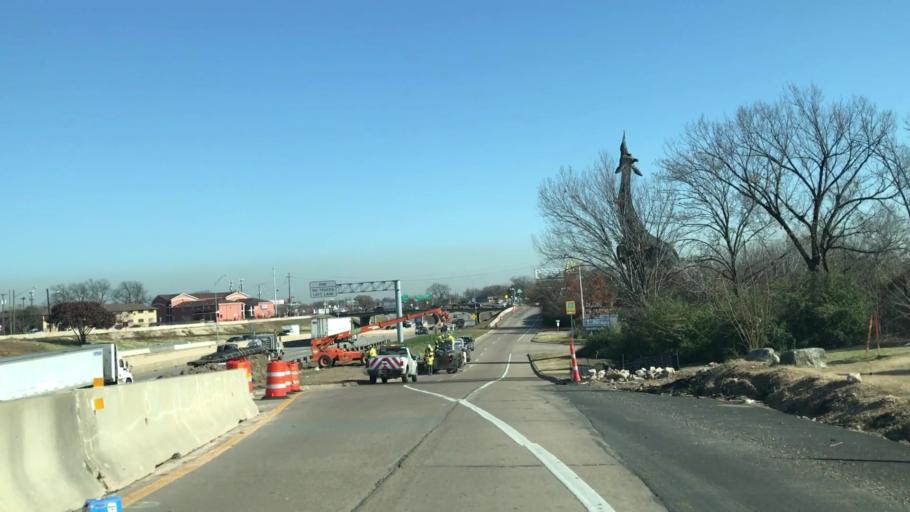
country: US
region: Texas
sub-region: Dallas County
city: Dallas
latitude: 32.7436
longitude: -96.8153
